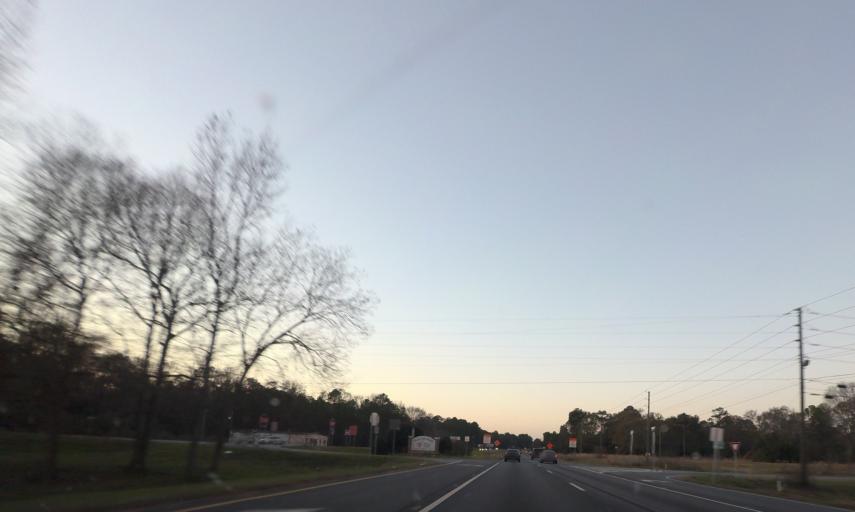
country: US
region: Georgia
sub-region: Houston County
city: Warner Robins
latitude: 32.6707
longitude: -83.6234
